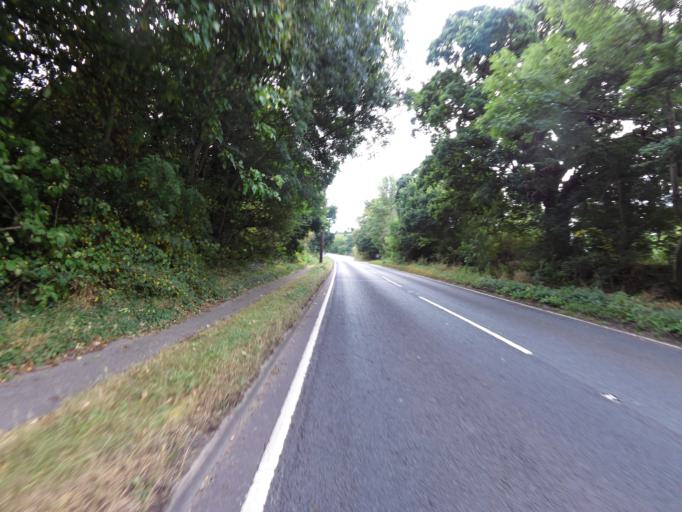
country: GB
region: England
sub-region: Hertfordshire
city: Shenley AV
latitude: 51.7124
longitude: -0.2987
